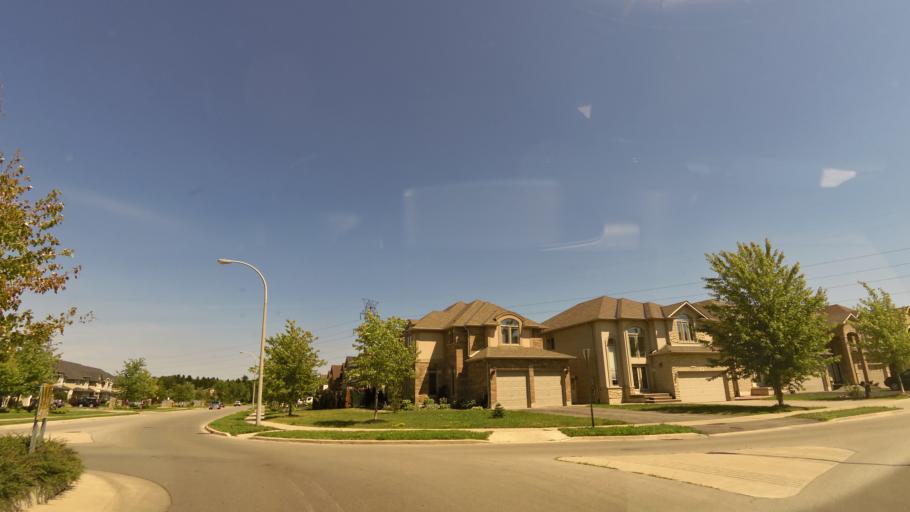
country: CA
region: Ontario
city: Ancaster
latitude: 43.2222
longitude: -79.9395
